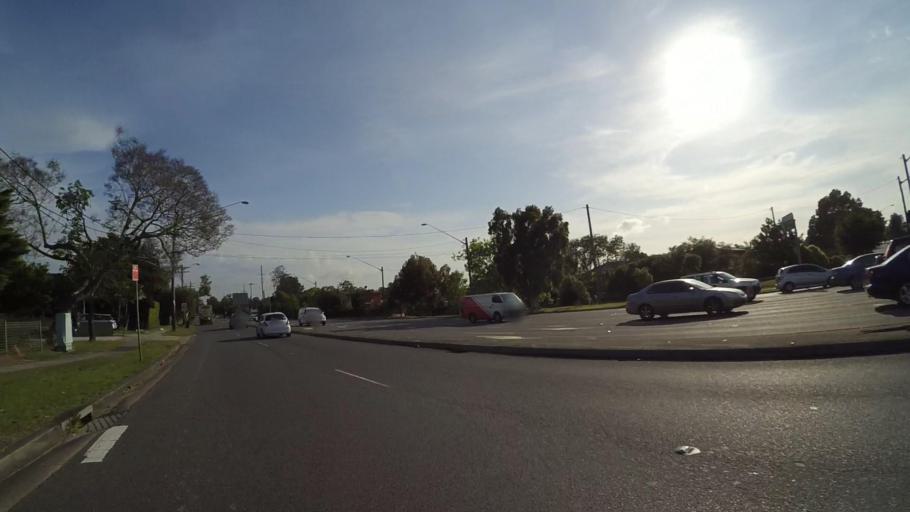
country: AU
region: New South Wales
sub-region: Sutherland Shire
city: Miranda
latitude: -34.0296
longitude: 151.1055
